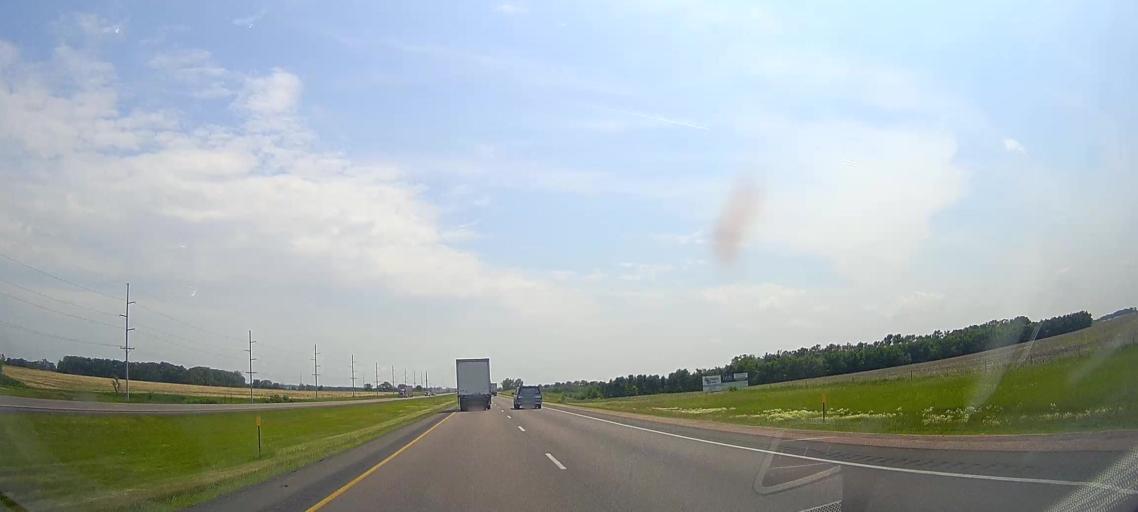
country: US
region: South Dakota
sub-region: Union County
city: Beresford
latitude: 43.1186
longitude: -96.7966
